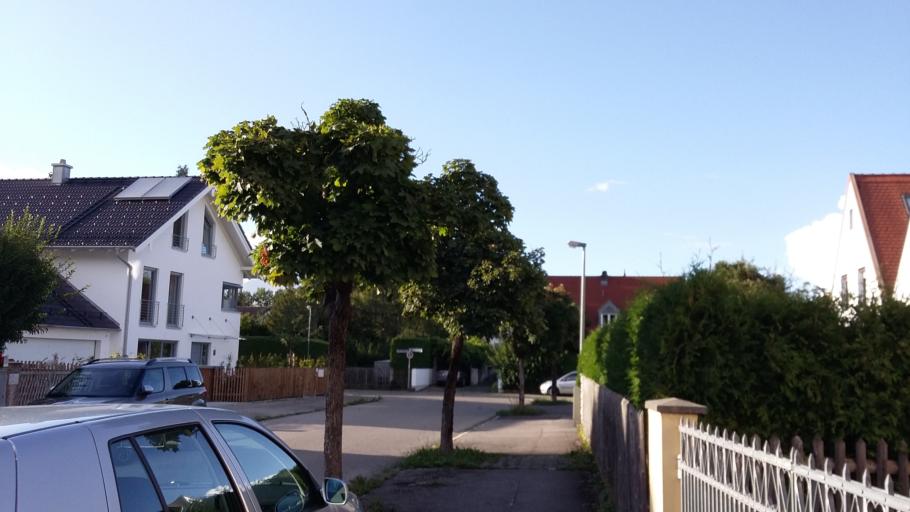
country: DE
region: Bavaria
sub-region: Upper Bavaria
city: Neuried
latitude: 48.0953
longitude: 11.4709
